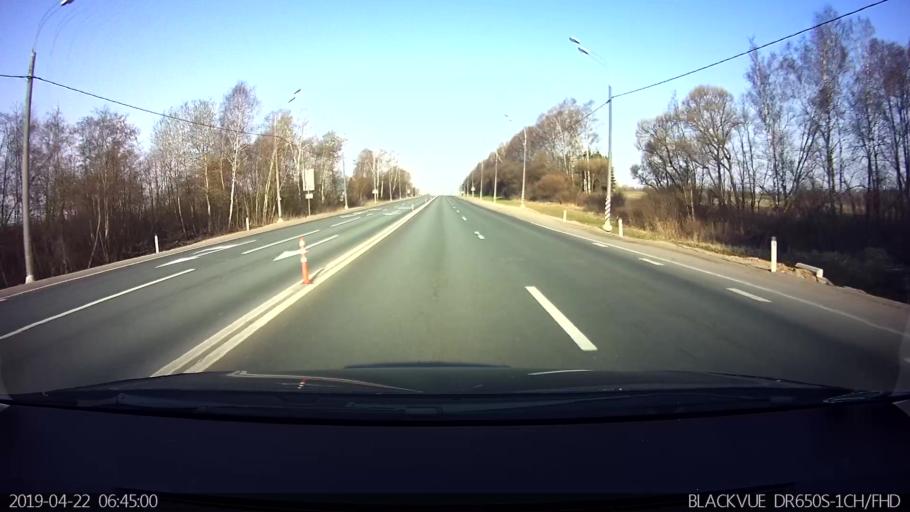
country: RU
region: Smolensk
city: Gagarin
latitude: 55.5031
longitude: 35.1503
